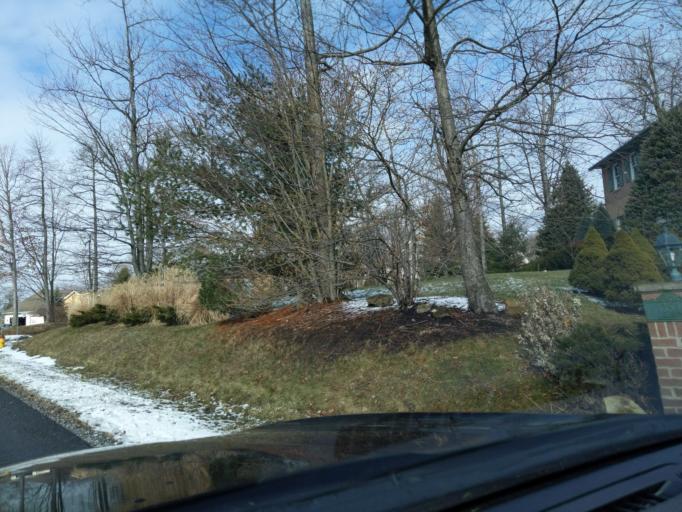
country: US
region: Pennsylvania
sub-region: Blair County
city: Lakemont
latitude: 40.4713
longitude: -78.3761
